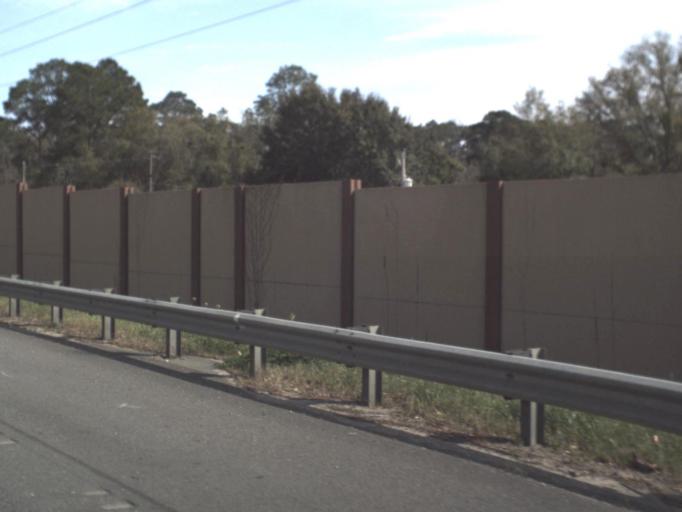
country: US
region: Florida
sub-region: Leon County
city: Tallahassee
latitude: 30.4781
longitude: -84.3440
